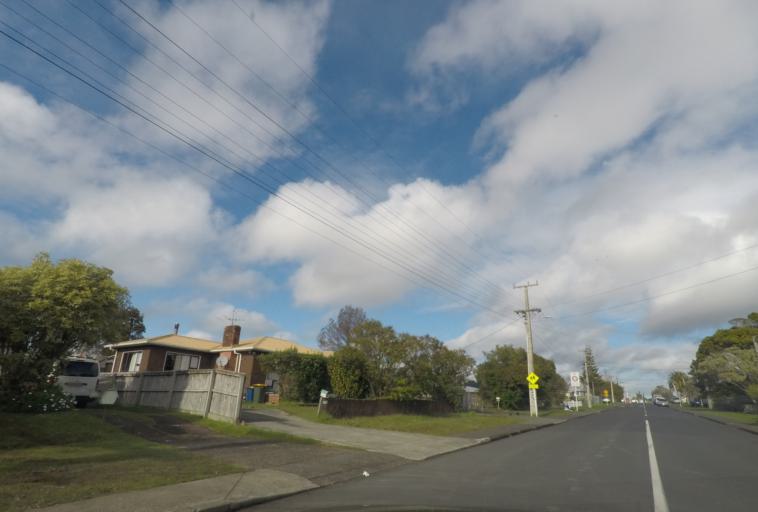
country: NZ
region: Auckland
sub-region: Auckland
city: Waitakere
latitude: -36.8970
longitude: 174.6651
